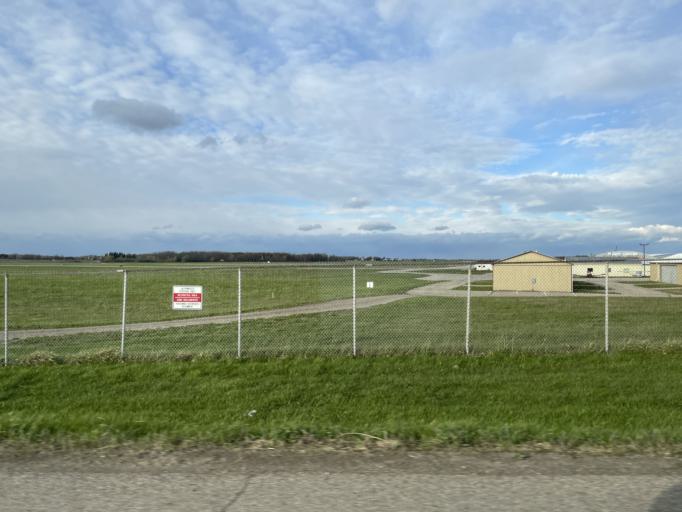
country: CA
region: Ontario
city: Kitchener
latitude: 43.4548
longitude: -80.3927
